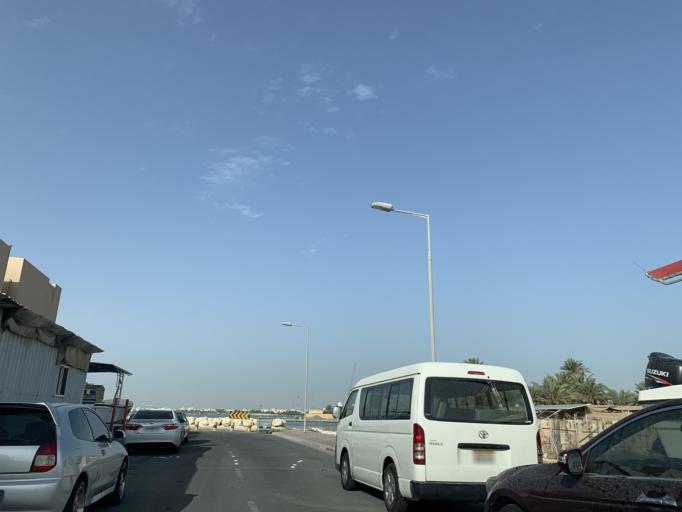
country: BH
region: Manama
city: Manama
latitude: 26.1797
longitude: 50.5884
